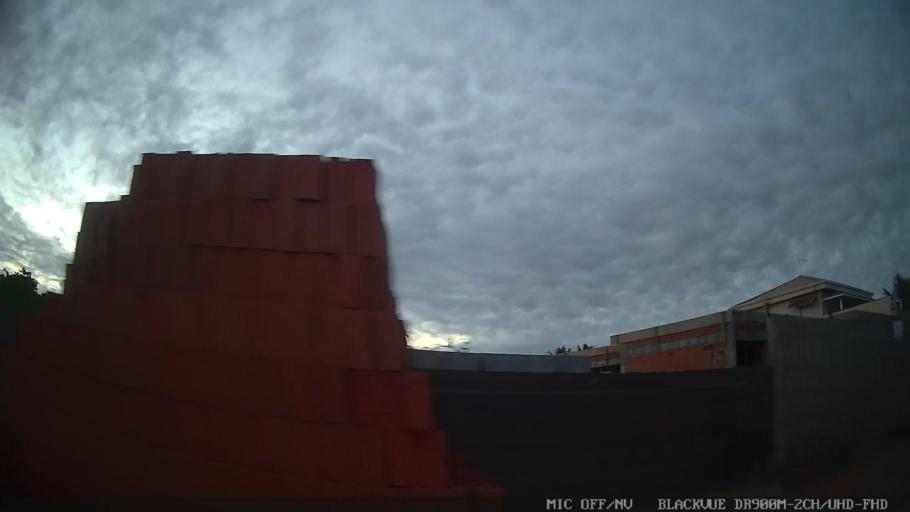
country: BR
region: Sao Paulo
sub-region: Itanhaem
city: Itanhaem
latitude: -24.2409
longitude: -46.8825
